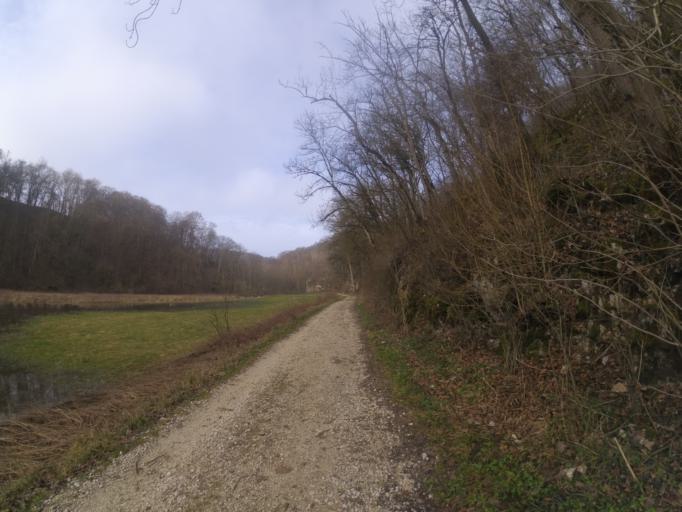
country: DE
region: Baden-Wuerttemberg
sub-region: Tuebingen Region
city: Rechtenstein
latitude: 48.2589
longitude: 9.5492
